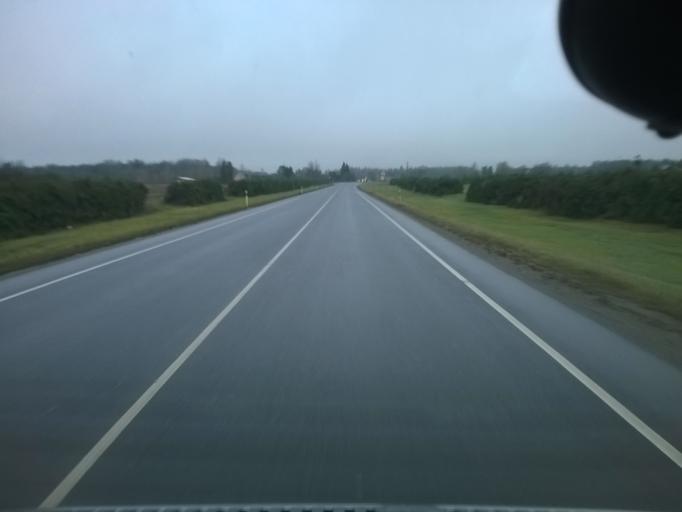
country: EE
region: Harju
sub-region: Saku vald
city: Saku
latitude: 59.3040
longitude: 24.7426
